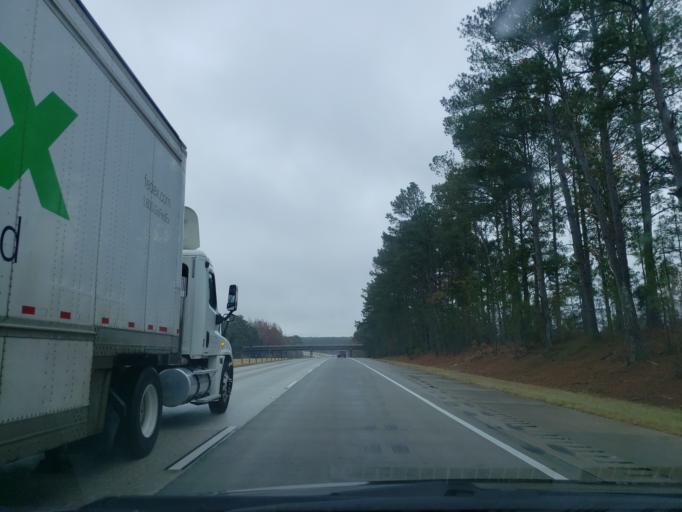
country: US
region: Georgia
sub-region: Treutlen County
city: Soperton
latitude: 32.4369
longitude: -82.7094
